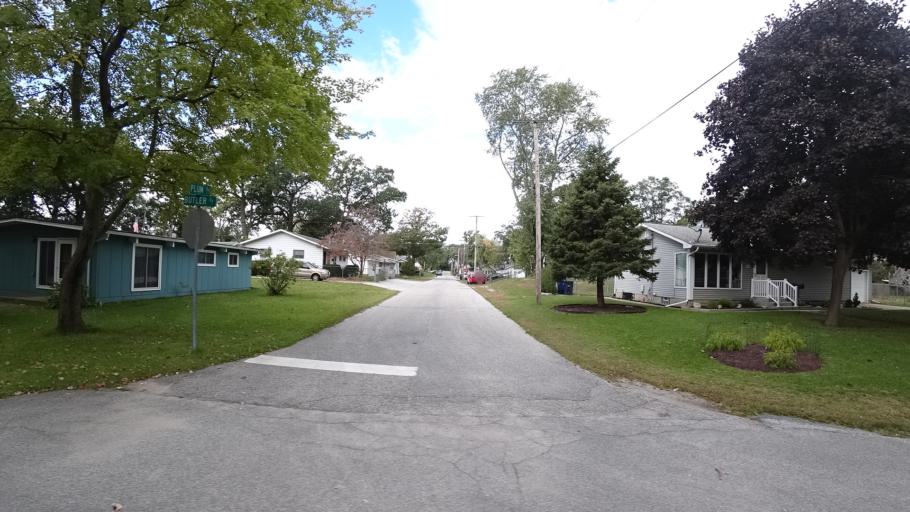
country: US
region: Indiana
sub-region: LaPorte County
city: Michigan City
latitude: 41.7047
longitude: -86.8772
